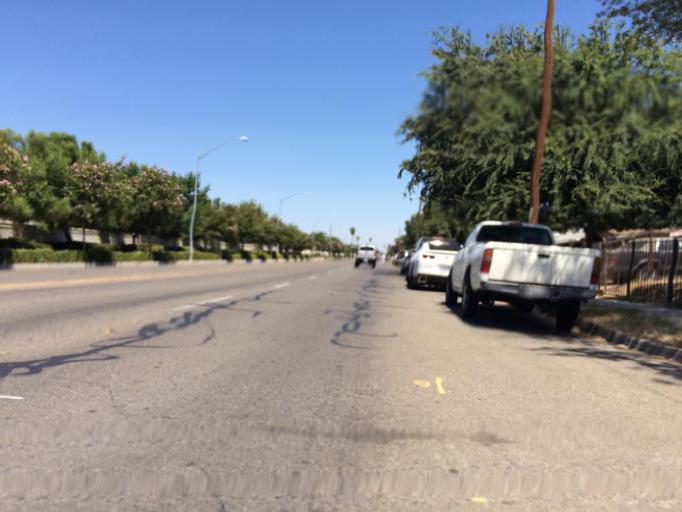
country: US
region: California
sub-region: Fresno County
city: Fresno
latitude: 36.7112
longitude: -119.7456
